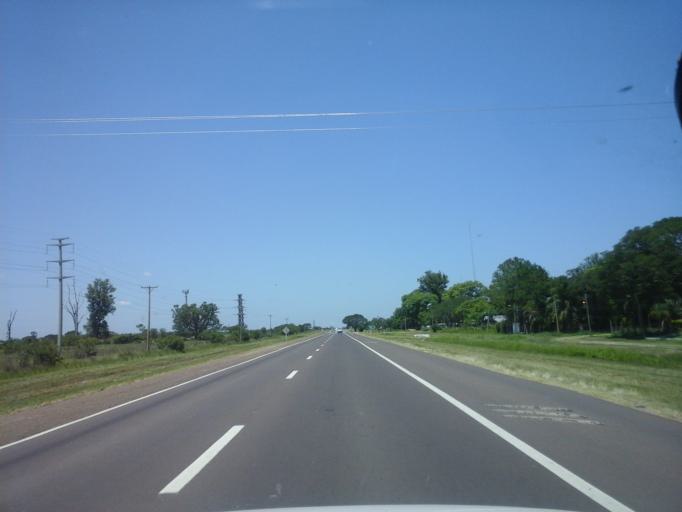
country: AR
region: Corrientes
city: Corrientes
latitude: -27.4269
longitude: -58.7176
